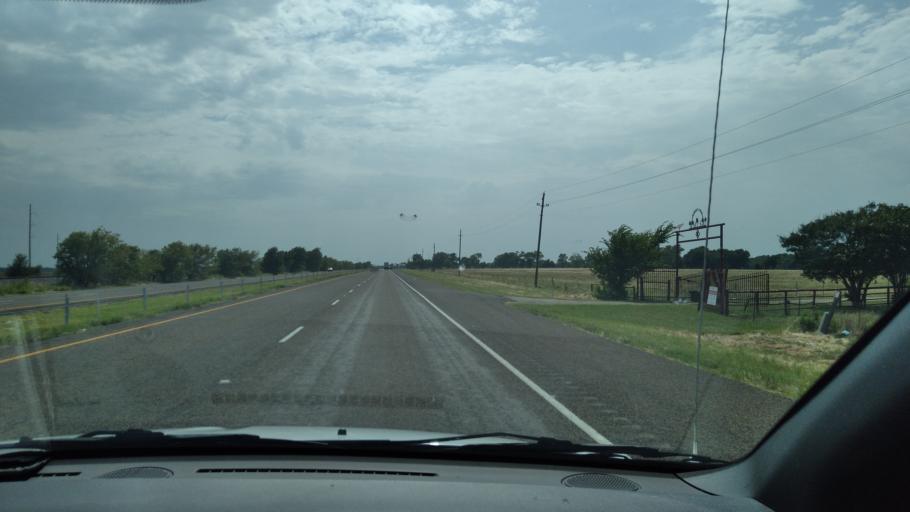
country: US
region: Texas
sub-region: Navarro County
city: Kerens
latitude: 32.1209
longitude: -96.3052
